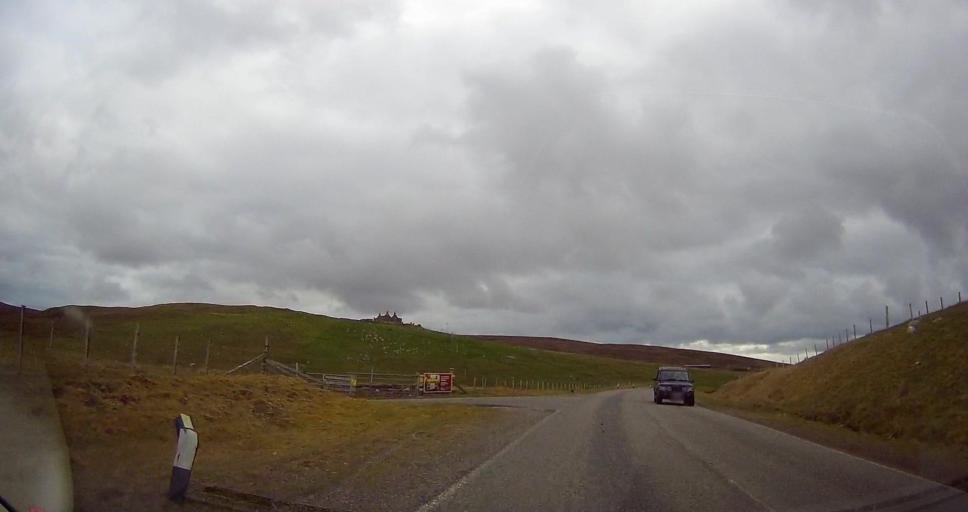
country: GB
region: Scotland
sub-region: Shetland Islands
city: Shetland
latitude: 60.6045
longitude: -1.1159
